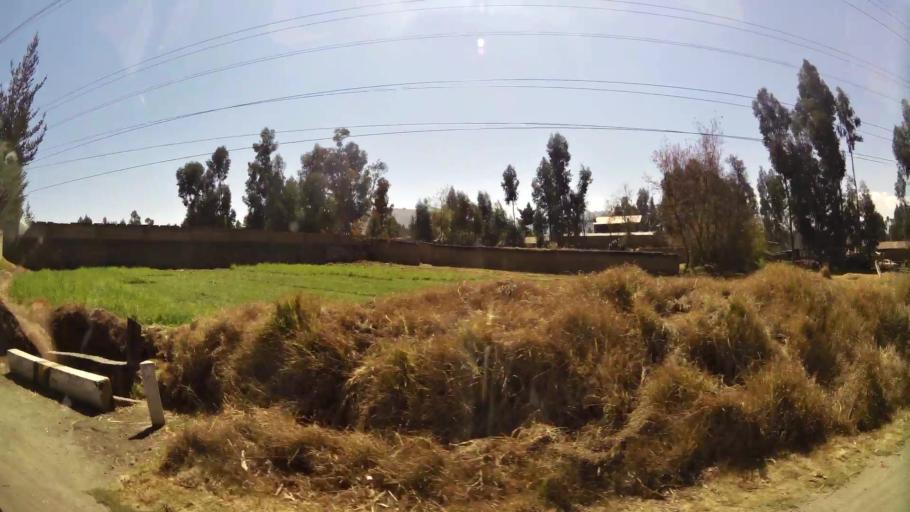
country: PE
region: Junin
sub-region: Provincia de Concepcion
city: Matahuasi
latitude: -11.8883
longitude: -75.3462
